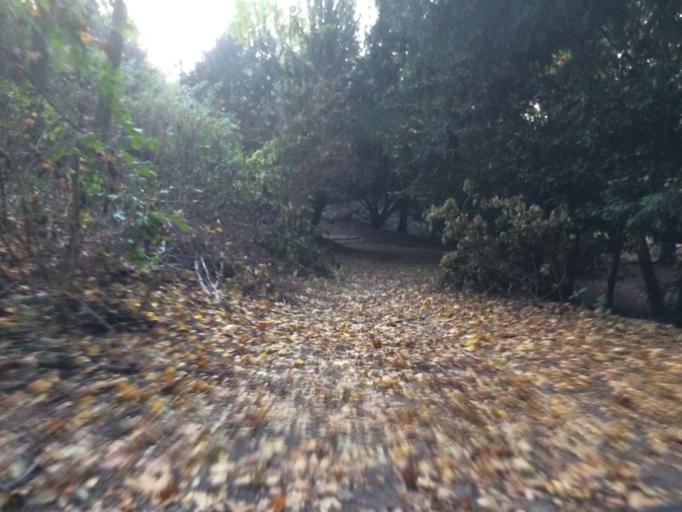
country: DE
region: Berlin
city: Gesundbrunnen
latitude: 52.5442
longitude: 13.3849
